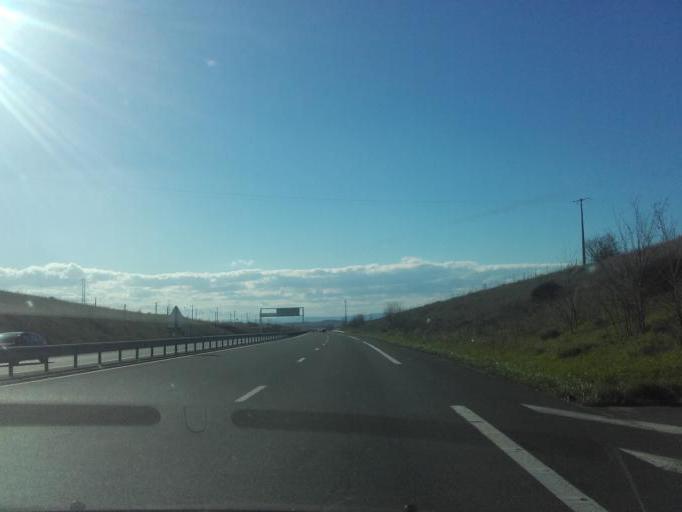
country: FR
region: Rhone-Alpes
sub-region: Departement de l'Ain
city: Beynost
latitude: 45.8560
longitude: 4.9963
